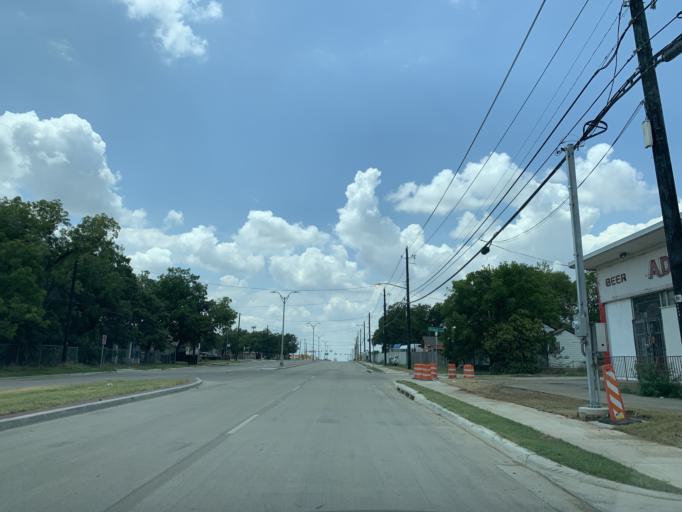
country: US
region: Texas
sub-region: Tarrant County
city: Forest Hill
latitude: 32.7313
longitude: -97.2579
